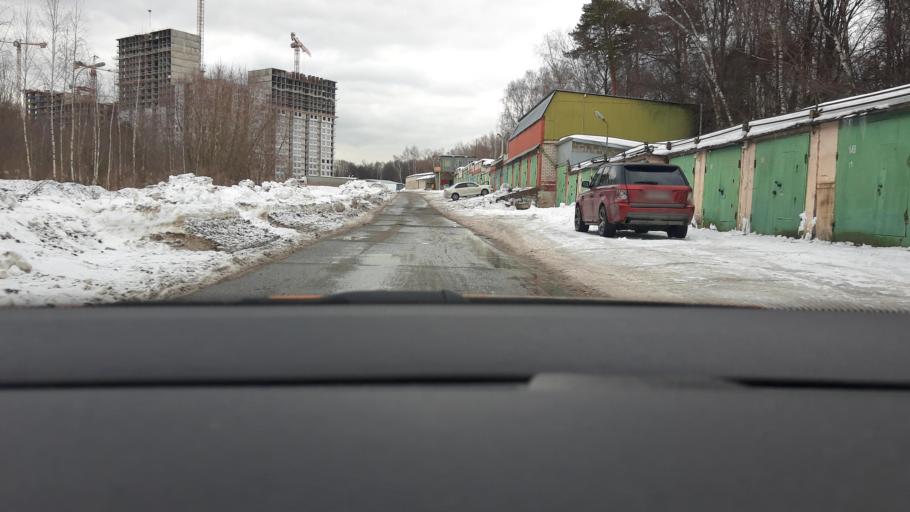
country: RU
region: Moscow
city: Babushkin
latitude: 55.8479
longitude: 37.7081
